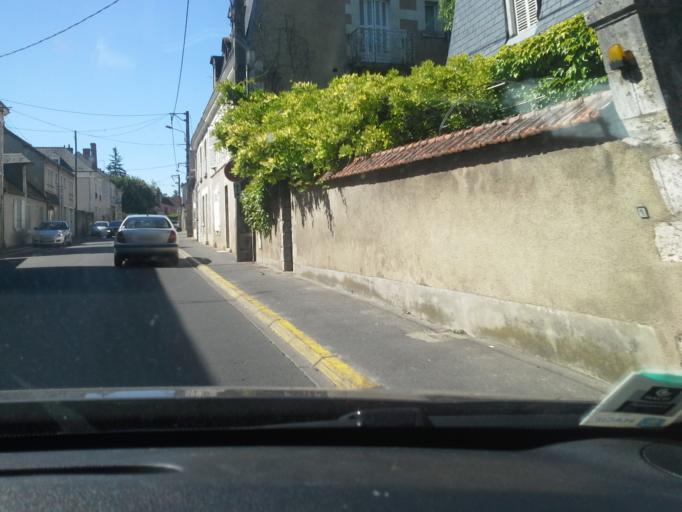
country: FR
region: Centre
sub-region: Departement du Loir-et-Cher
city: Cellettes
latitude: 47.5262
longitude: 1.3825
